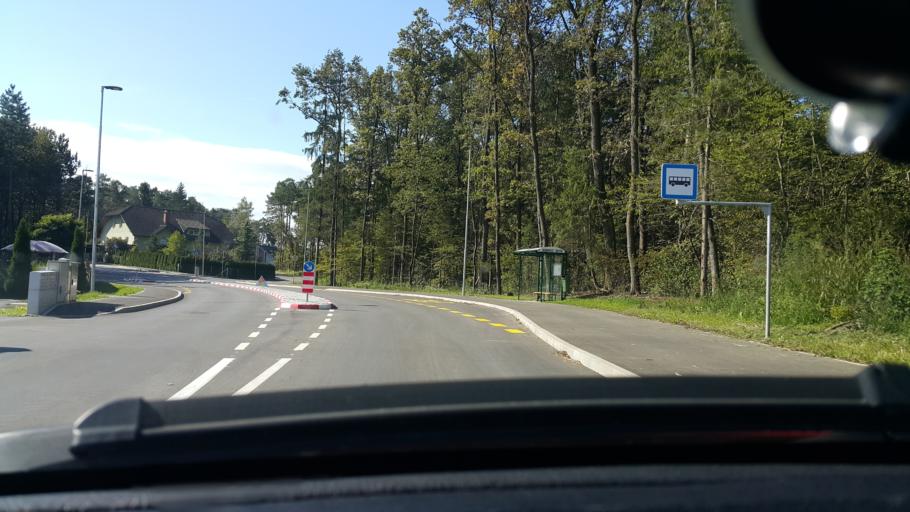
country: SI
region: Miklavz na Dravskem Polju
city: Miklavz na Dravskem Polju
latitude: 46.4878
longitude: 15.7008
